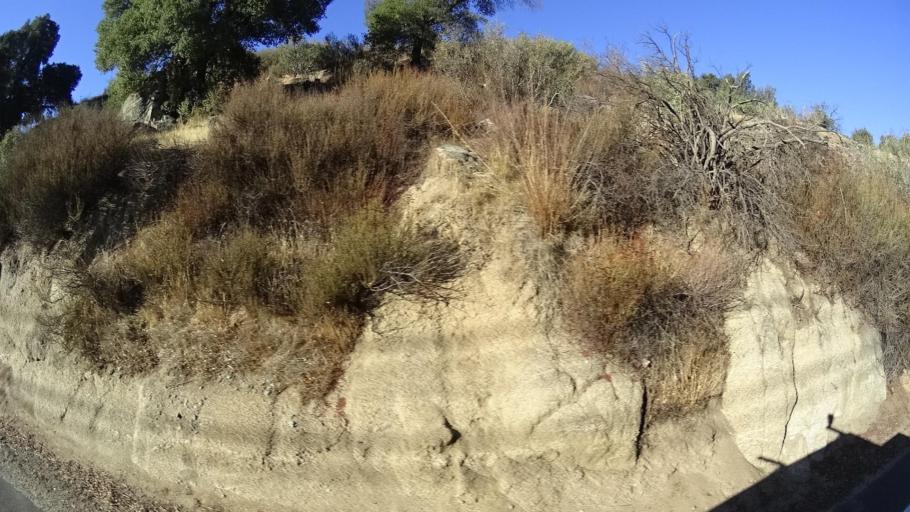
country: US
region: California
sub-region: San Diego County
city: Campo
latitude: 32.6118
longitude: -116.4751
